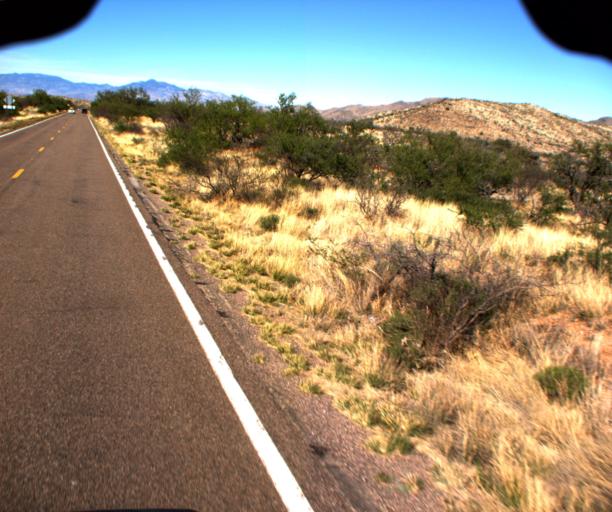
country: US
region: Arizona
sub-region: Pima County
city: Corona de Tucson
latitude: 31.8525
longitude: -110.6967
